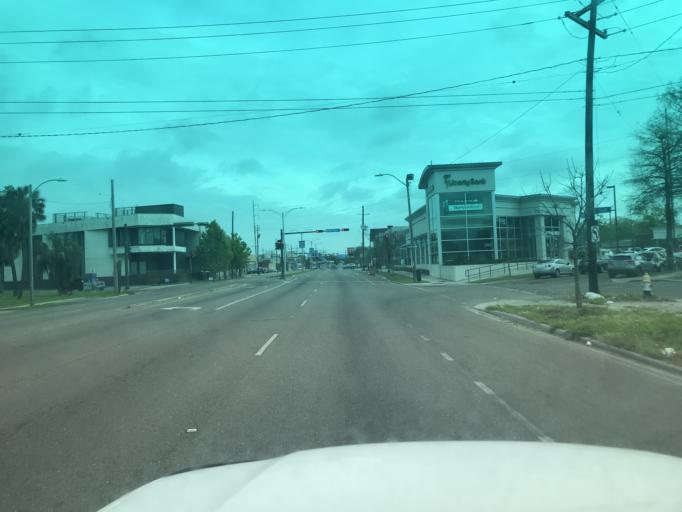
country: US
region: Louisiana
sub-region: Orleans Parish
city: New Orleans
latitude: 29.9966
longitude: -90.0618
